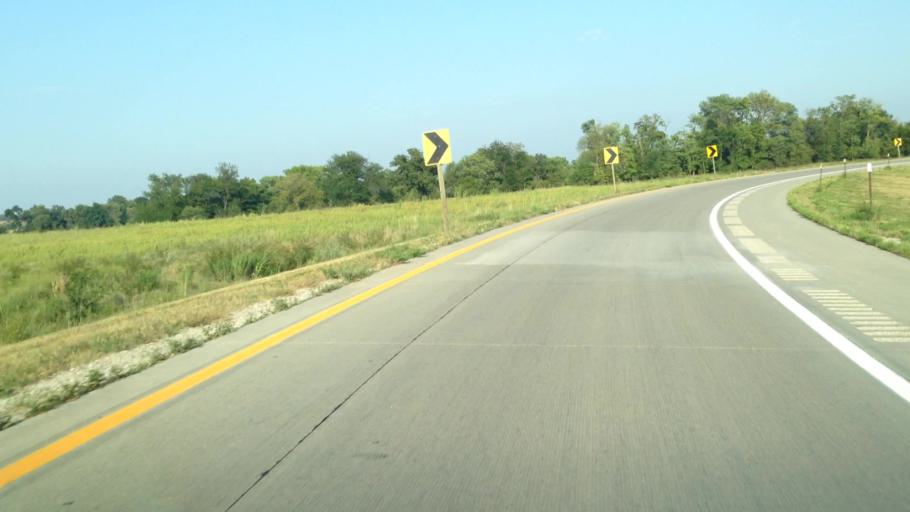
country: US
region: Kansas
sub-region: Franklin County
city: Ottawa
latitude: 38.6389
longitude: -95.2180
